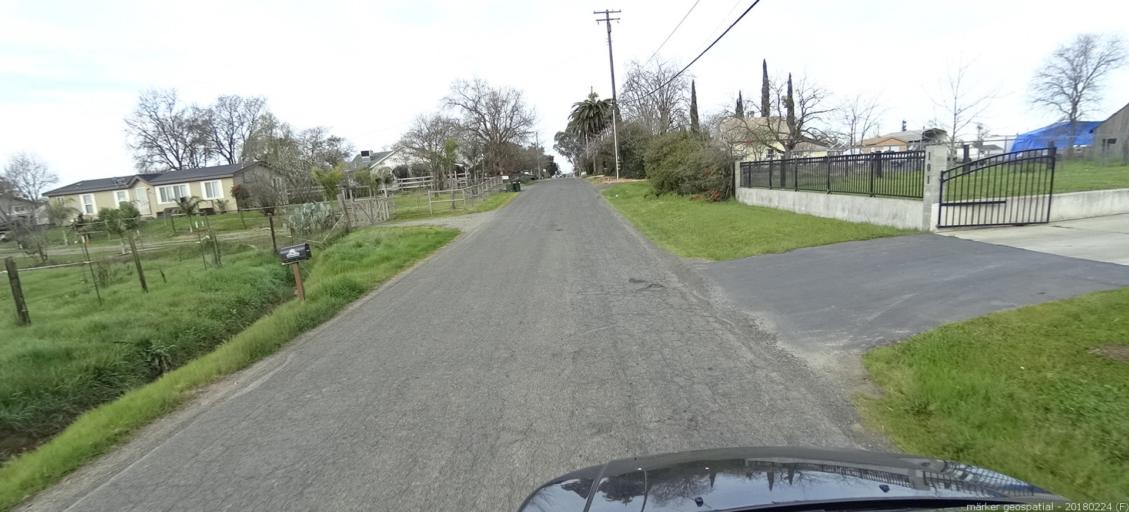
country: US
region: California
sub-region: Sacramento County
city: Rio Linda
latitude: 38.6768
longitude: -121.4636
